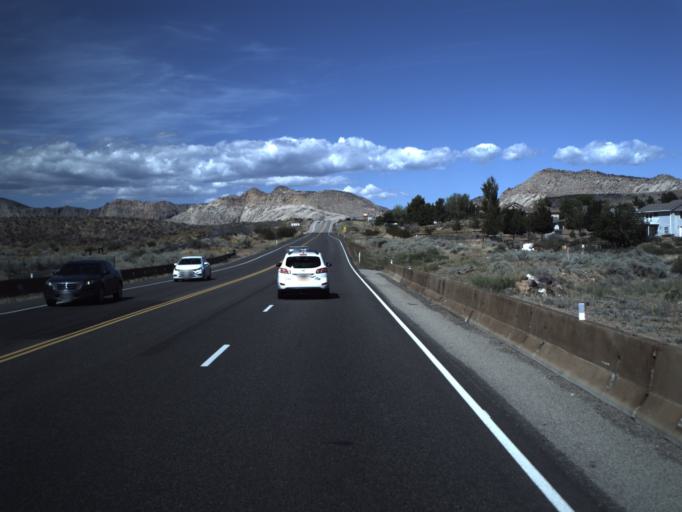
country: US
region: Utah
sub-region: Washington County
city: Ivins
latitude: 37.2009
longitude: -113.6254
